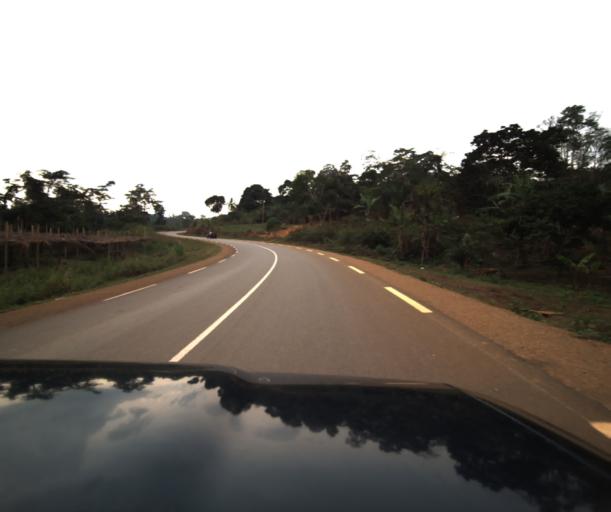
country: CM
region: Centre
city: Mbankomo
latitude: 3.7771
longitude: 11.4173
